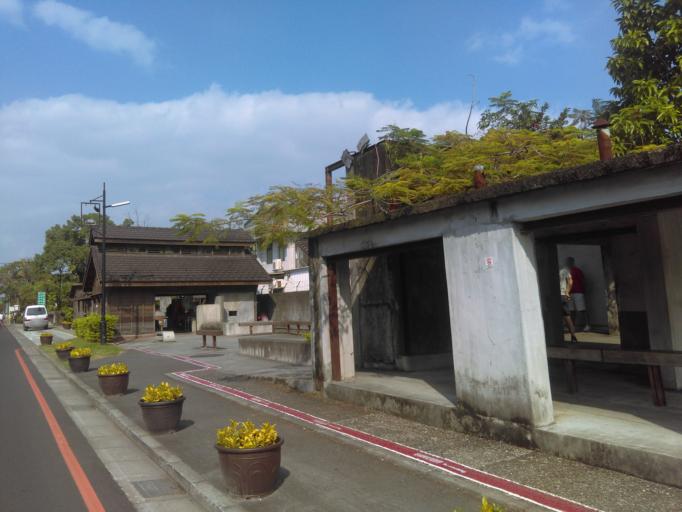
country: TW
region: Taiwan
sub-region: Yilan
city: Yilan
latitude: 24.7533
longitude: 121.7570
